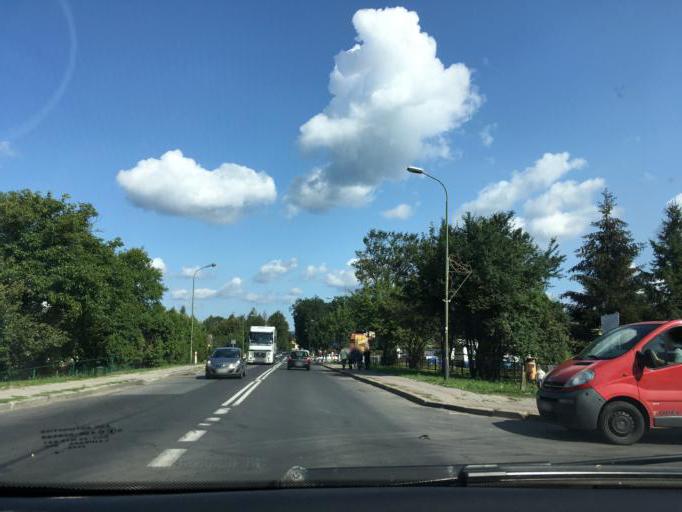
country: PL
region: Subcarpathian Voivodeship
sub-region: Powiat leski
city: Lesko
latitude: 49.4755
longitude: 22.3249
